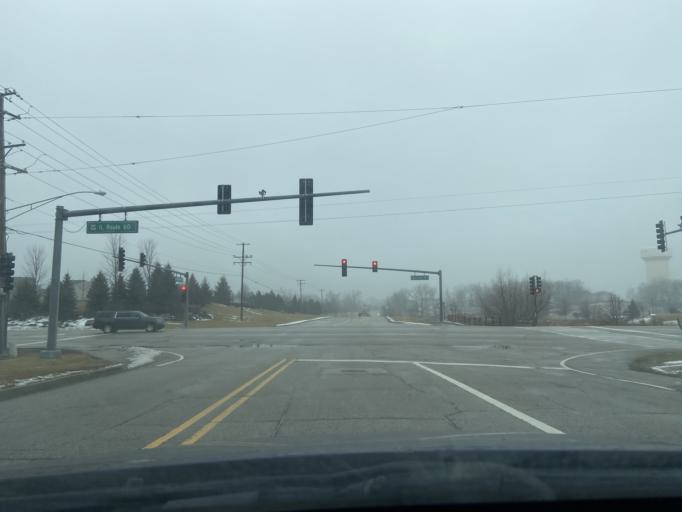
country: US
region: Illinois
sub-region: Lake County
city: Volo
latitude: 42.3214
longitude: -88.1451
